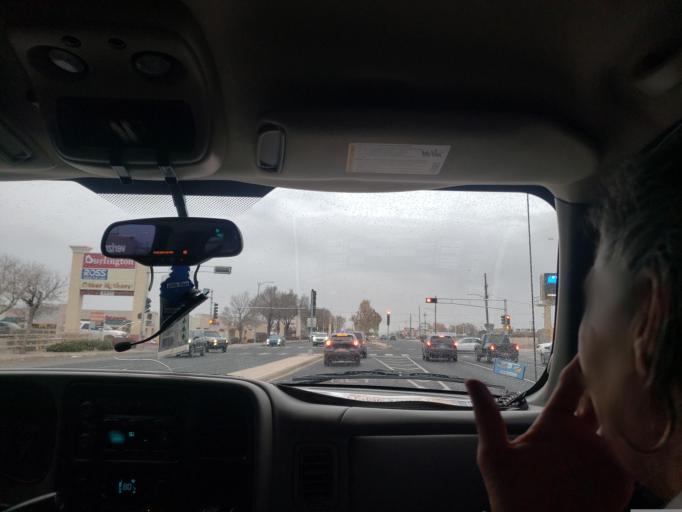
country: US
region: New Mexico
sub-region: Bernalillo County
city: North Valley
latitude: 35.1323
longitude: -106.5865
